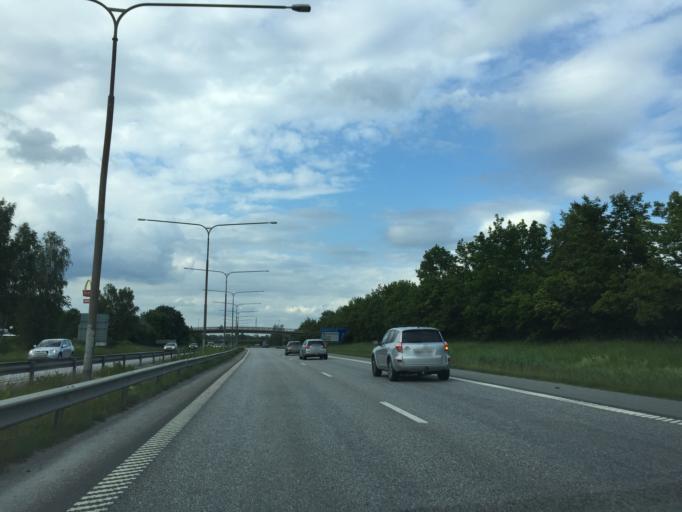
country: SE
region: OErebro
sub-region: Orebro Kommun
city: Orebro
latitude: 59.2715
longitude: 15.1773
